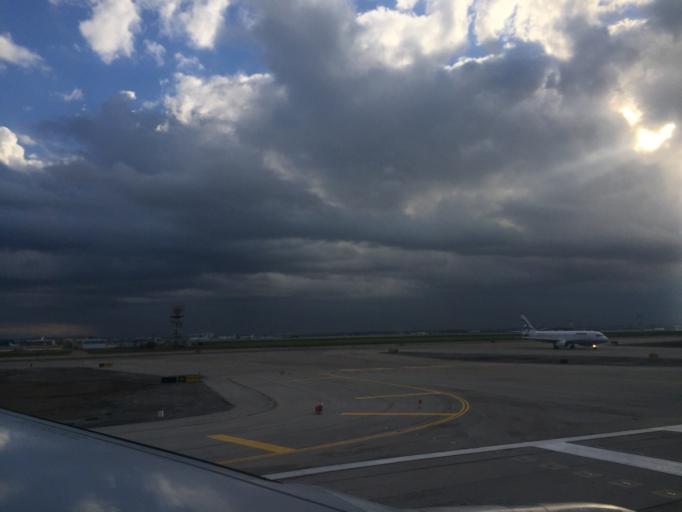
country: IL
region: Central District
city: Yehud
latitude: 32.0178
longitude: 34.8935
